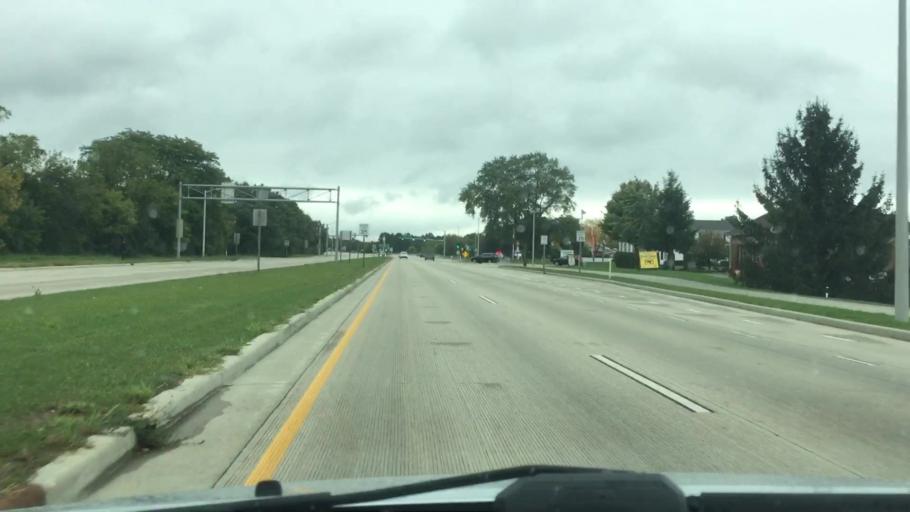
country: US
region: Wisconsin
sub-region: Waukesha County
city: Oconomowoc
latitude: 43.0947
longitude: -88.4796
